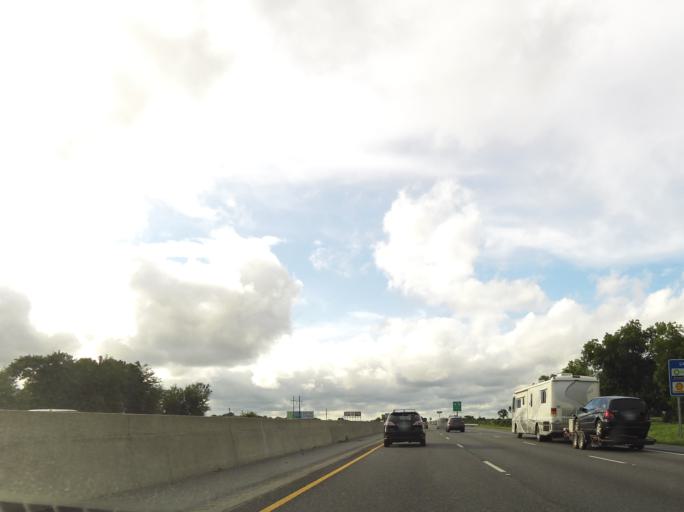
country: US
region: Georgia
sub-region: Turner County
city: Ashburn
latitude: 31.6924
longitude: -83.6286
